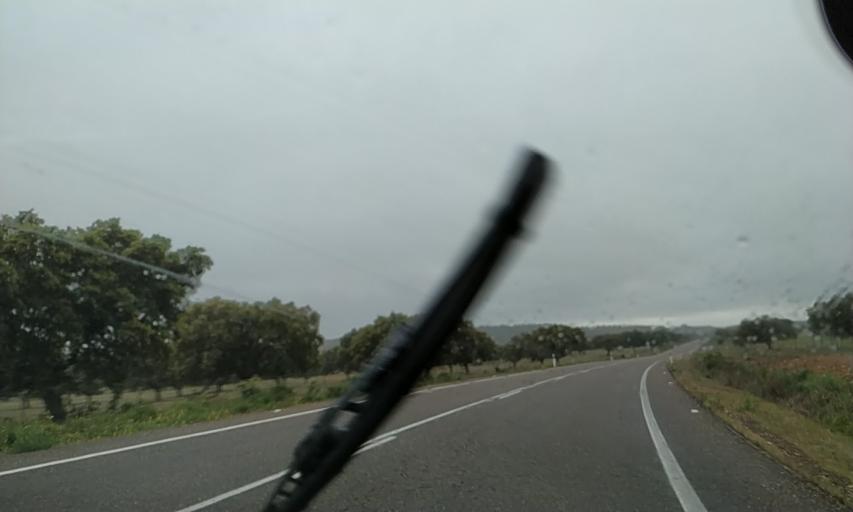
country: ES
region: Extremadura
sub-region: Provincia de Badajoz
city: La Roca de la Sierra
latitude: 39.0964
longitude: -6.7135
